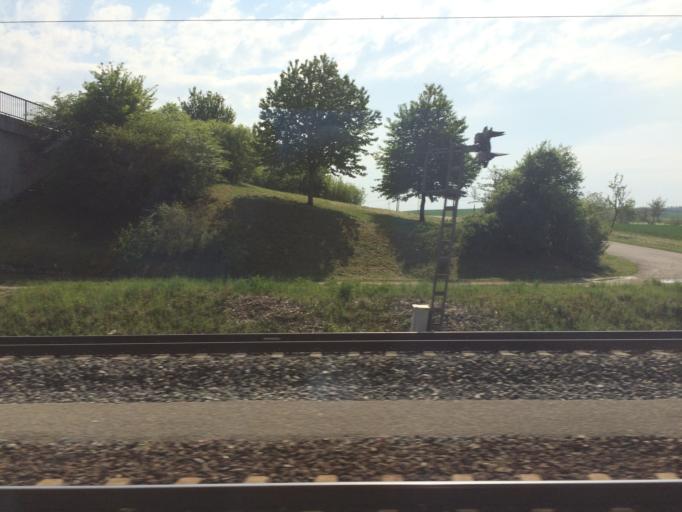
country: DE
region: Bavaria
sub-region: Regierungsbezirk Unterfranken
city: Markt Einersheim
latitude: 49.6867
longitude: 10.2806
